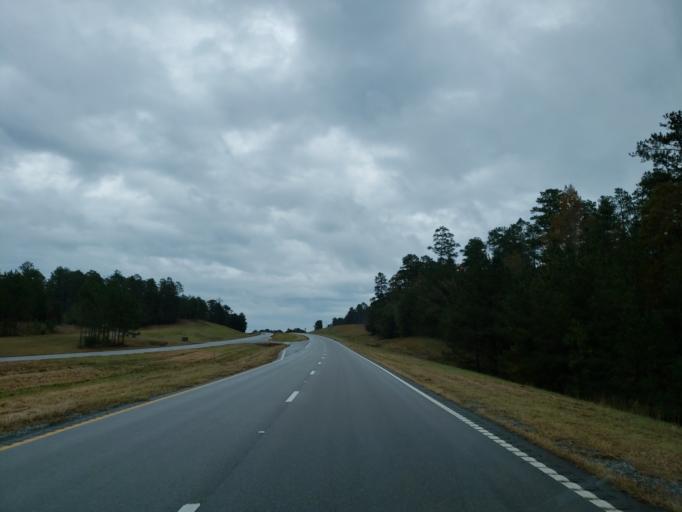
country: US
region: Mississippi
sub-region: Wayne County
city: Waynesboro
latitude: 31.6857
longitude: -88.7014
